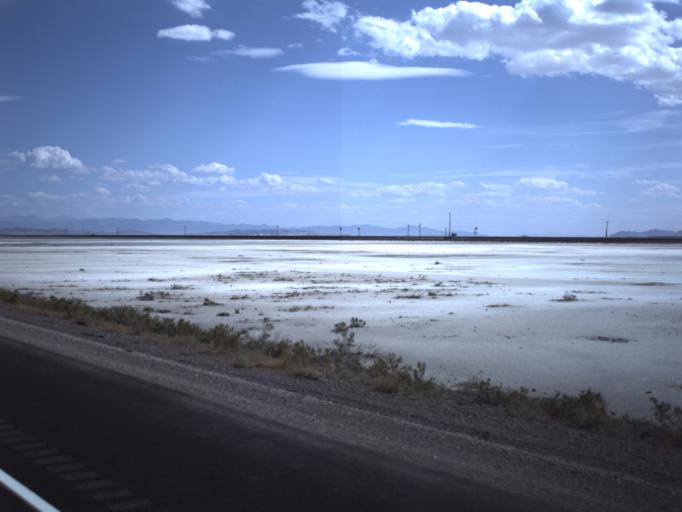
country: US
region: Utah
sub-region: Tooele County
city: Wendover
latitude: 40.7310
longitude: -113.5038
